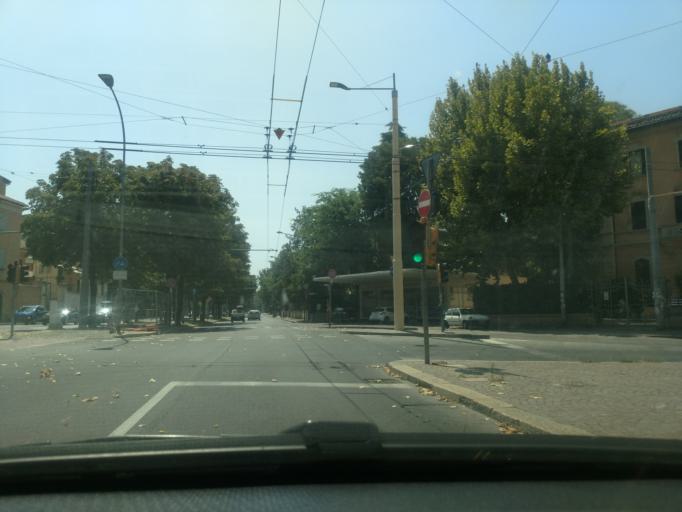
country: IT
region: Emilia-Romagna
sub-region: Provincia di Bologna
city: Bologna
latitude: 44.4901
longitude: 11.3575
